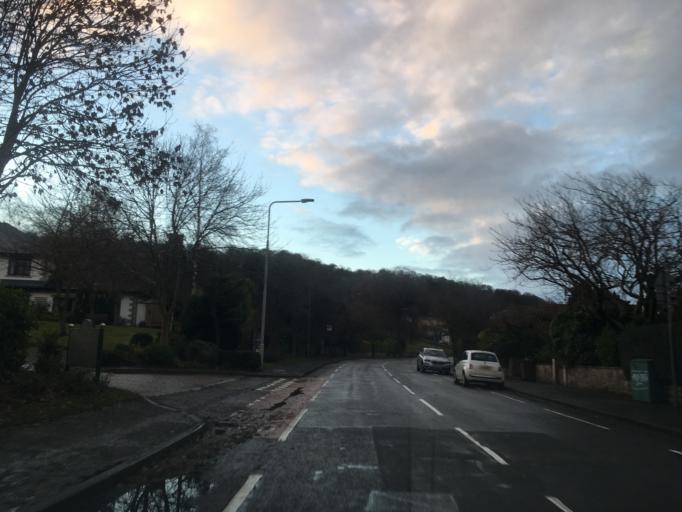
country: GB
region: Scotland
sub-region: Edinburgh
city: Colinton
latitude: 55.9558
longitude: -3.2627
